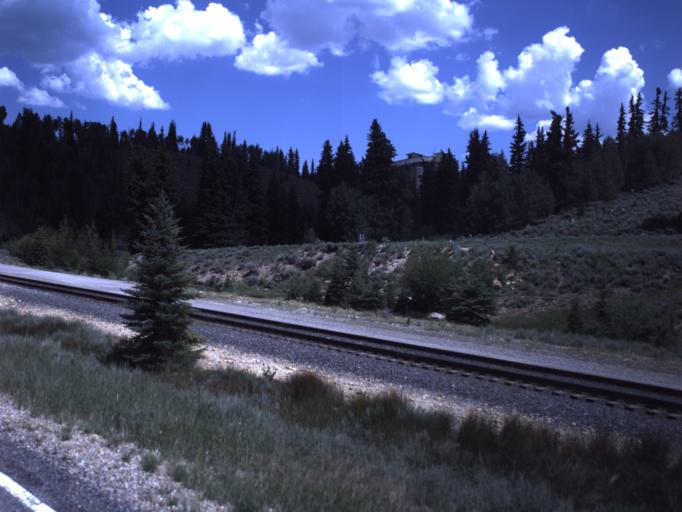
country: US
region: Utah
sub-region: Sanpete County
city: Fairview
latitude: 39.6787
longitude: -111.1584
